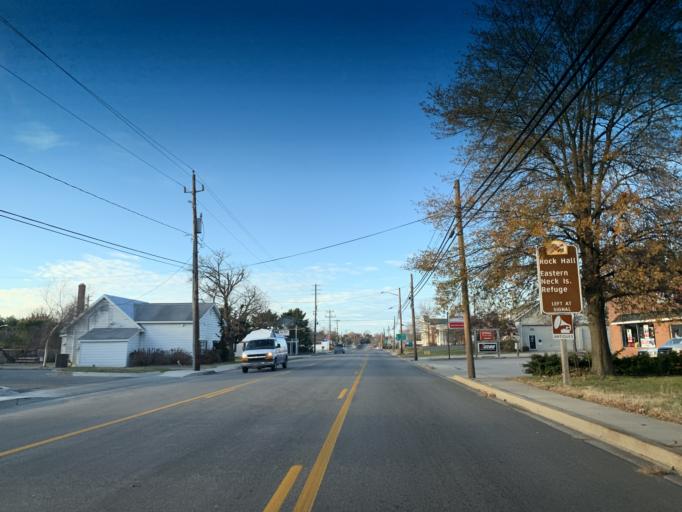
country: US
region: Maryland
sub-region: Kent County
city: Chestertown
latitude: 39.2211
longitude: -76.0684
